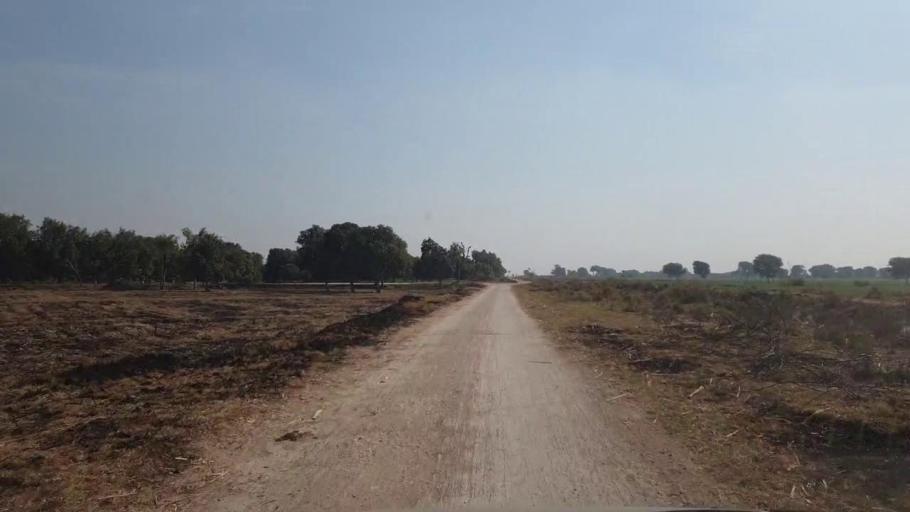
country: PK
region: Sindh
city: Chambar
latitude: 25.3589
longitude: 68.8030
